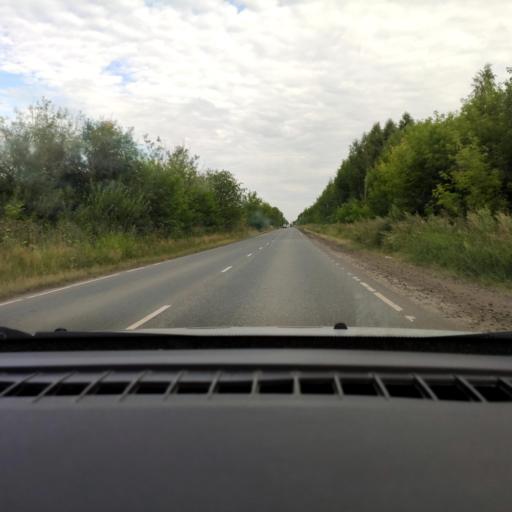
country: RU
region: Perm
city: Gamovo
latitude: 57.8980
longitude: 56.1815
